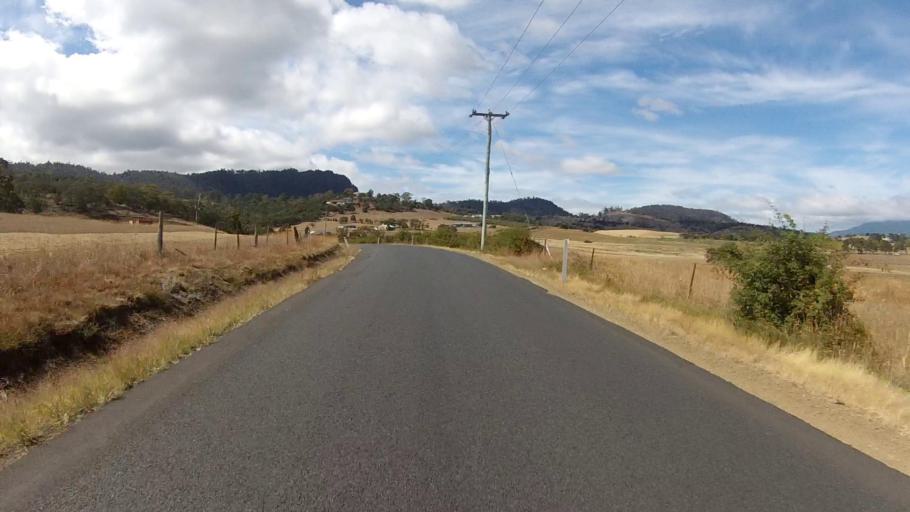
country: AU
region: Tasmania
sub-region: Brighton
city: Old Beach
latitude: -42.7511
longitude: 147.3028
